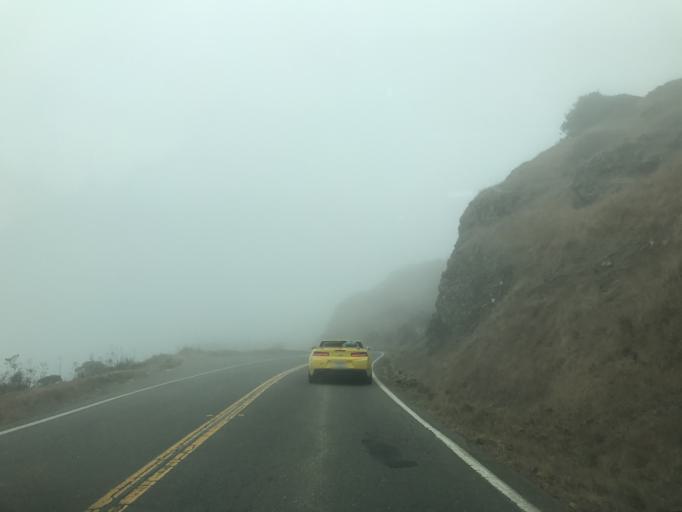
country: US
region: California
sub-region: Sonoma County
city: Monte Rio
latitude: 38.4750
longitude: -123.1585
